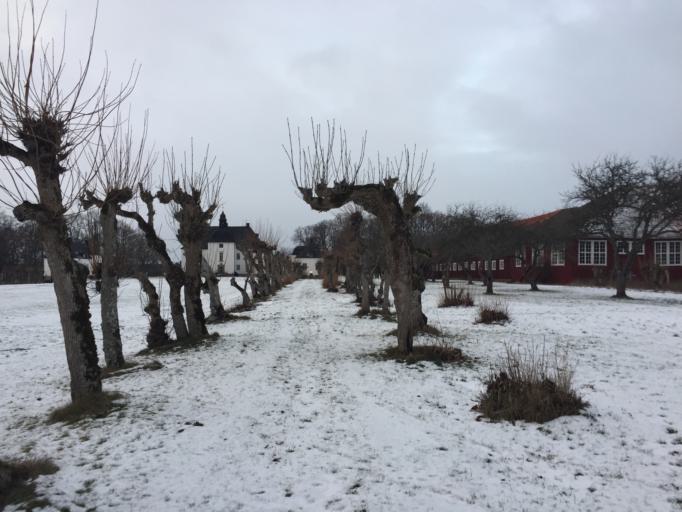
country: SE
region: Stockholm
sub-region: Haninge Kommun
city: Haninge
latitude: 59.1066
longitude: 18.1978
